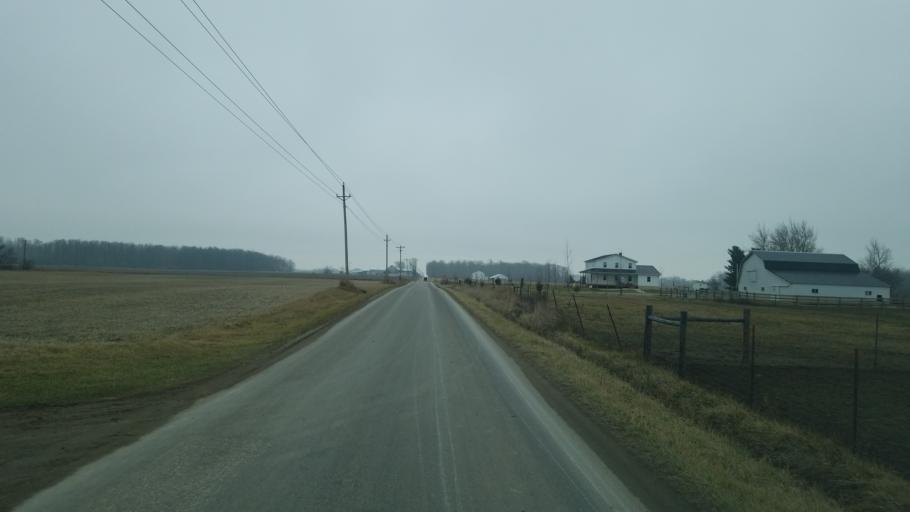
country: US
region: Indiana
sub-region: Adams County
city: Berne
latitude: 40.6314
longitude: -84.9069
